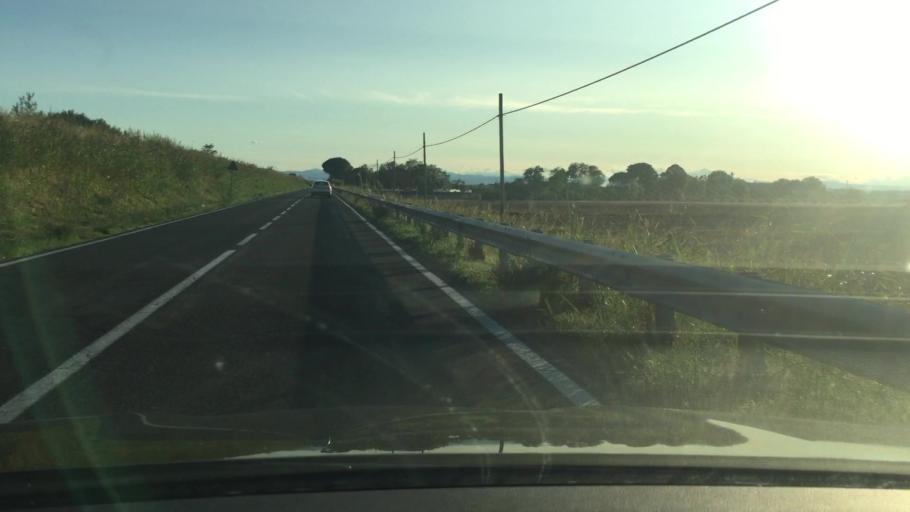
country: IT
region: Emilia-Romagna
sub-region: Provincia di Ravenna
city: Savio
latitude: 44.2998
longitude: 12.2796
